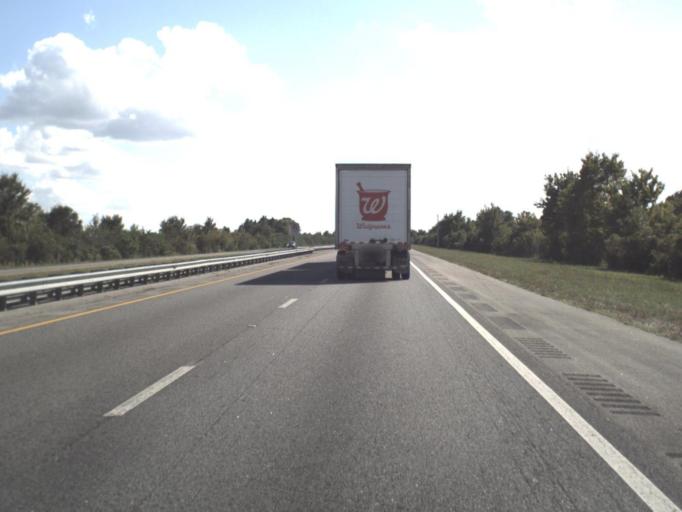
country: US
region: Florida
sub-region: Brevard County
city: June Park
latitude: 27.8379
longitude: -81.0060
